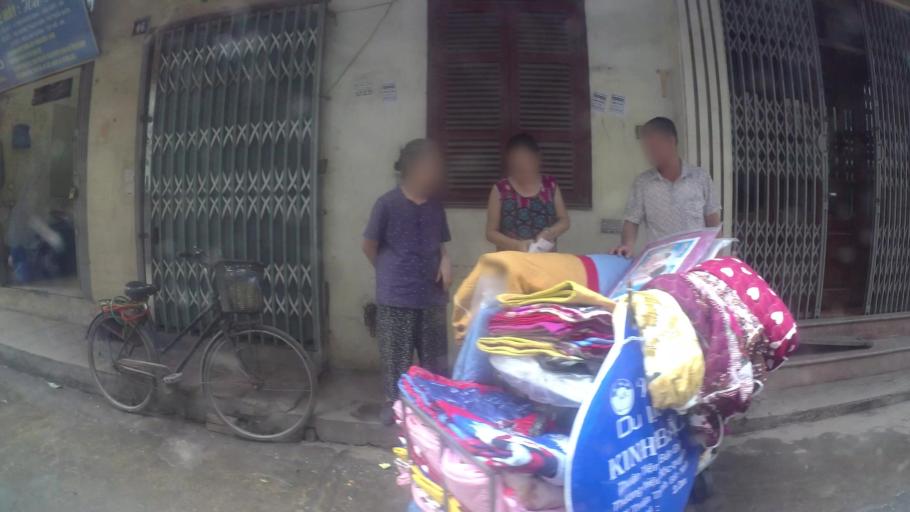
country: VN
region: Ha Noi
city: Hoan Kiem
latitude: 21.0506
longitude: 105.8428
